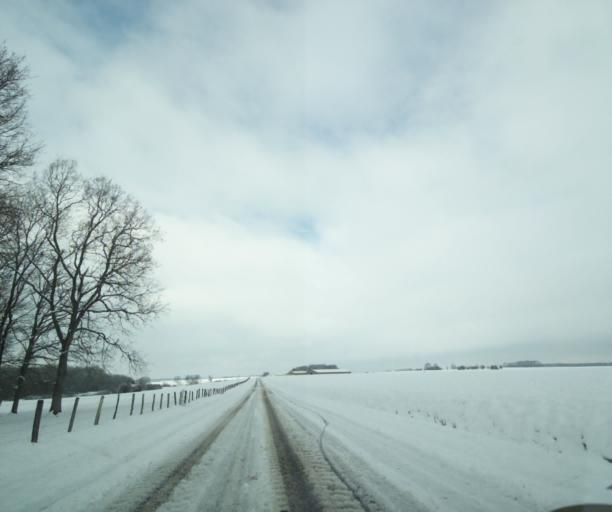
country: FR
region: Champagne-Ardenne
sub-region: Departement de la Haute-Marne
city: Montier-en-Der
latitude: 48.5163
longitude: 4.6807
